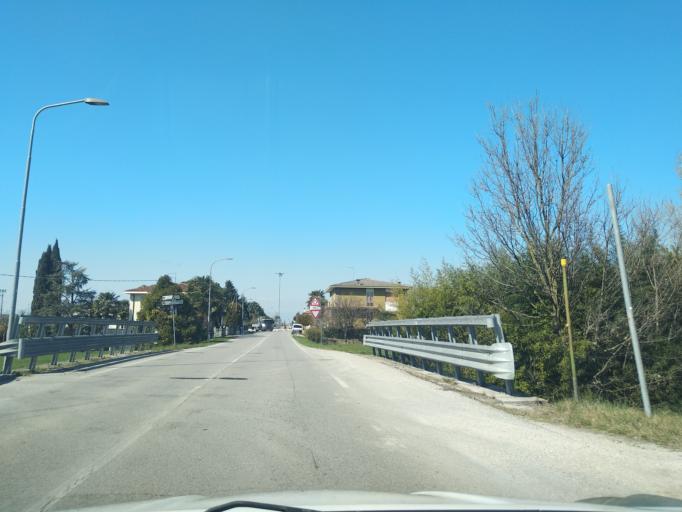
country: IT
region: Veneto
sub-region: Provincia di Padova
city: Taggi
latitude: 45.4730
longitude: 11.8127
